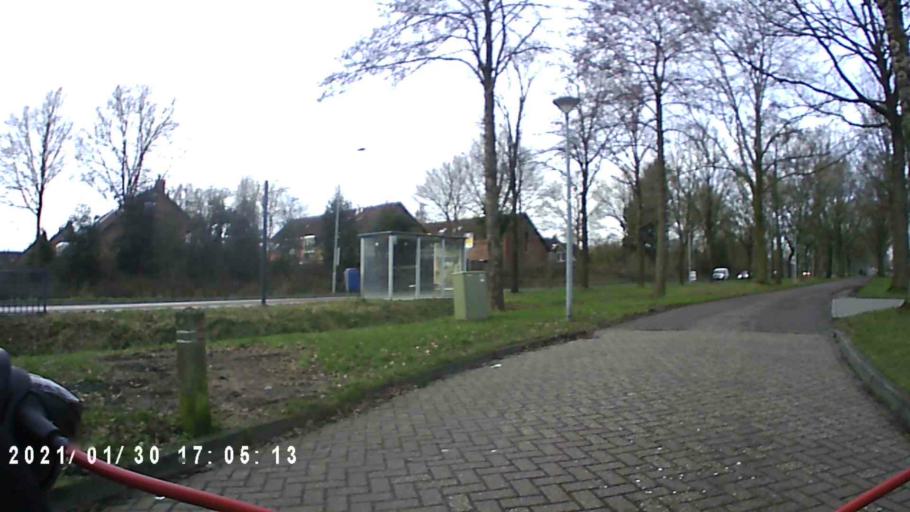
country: NL
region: Groningen
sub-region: Gemeente Leek
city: Leek
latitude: 53.1578
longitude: 6.3692
